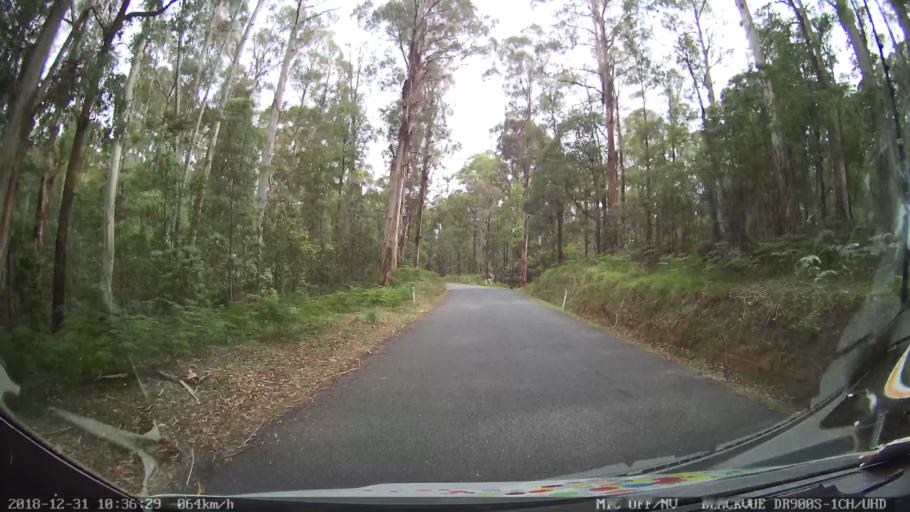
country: AU
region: New South Wales
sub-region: Snowy River
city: Jindabyne
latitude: -36.4258
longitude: 148.1714
